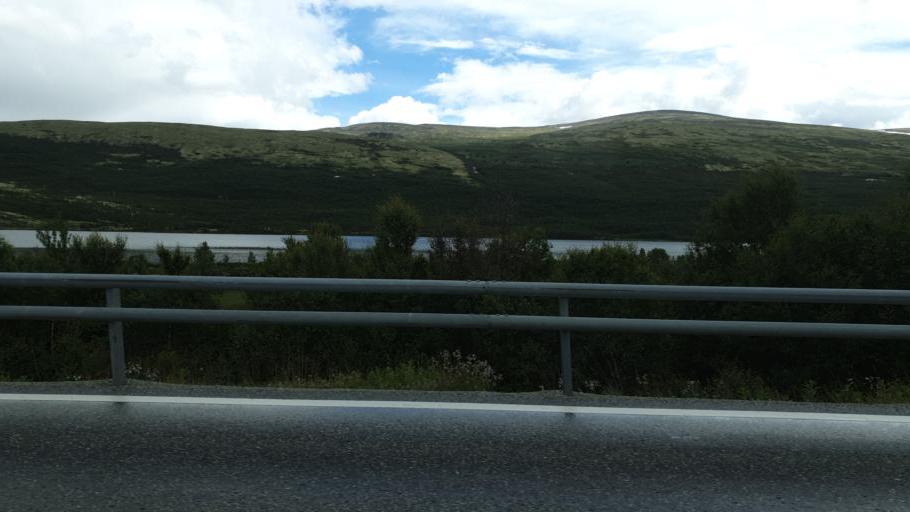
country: NO
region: Oppland
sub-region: Dovre
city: Dovre
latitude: 62.1793
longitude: 9.4702
